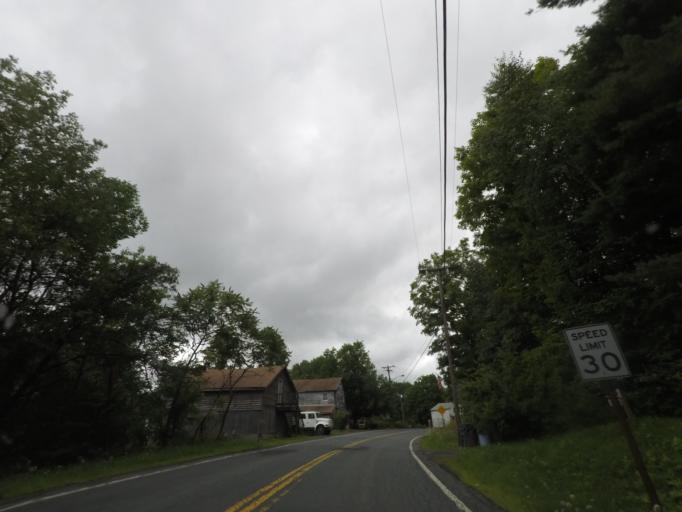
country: US
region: New York
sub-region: Rensselaer County
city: Poestenkill
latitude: 42.6832
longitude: -73.4944
